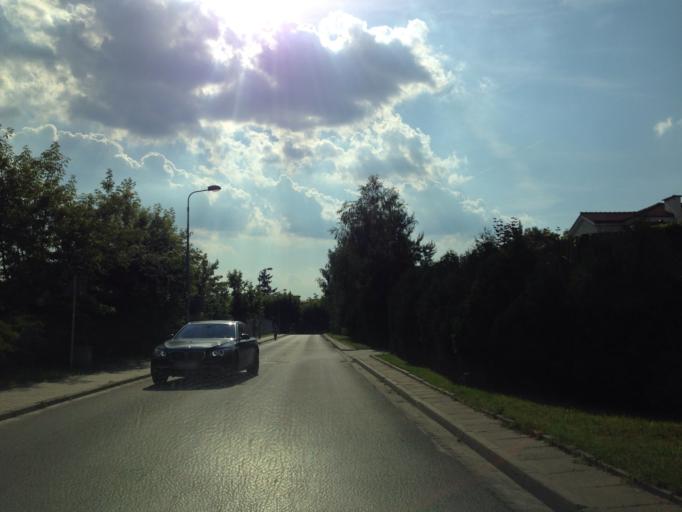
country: PL
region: Masovian Voivodeship
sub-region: Warszawa
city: Bemowo
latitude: 52.2580
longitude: 20.8955
